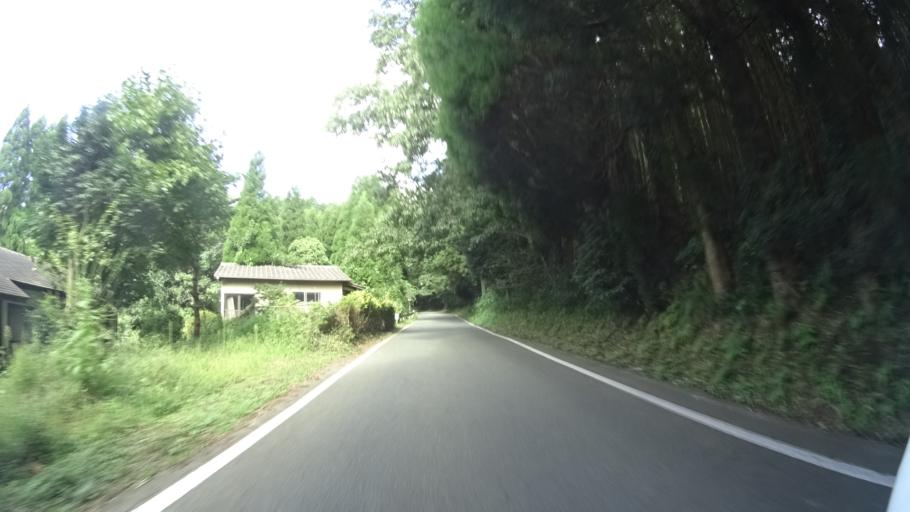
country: JP
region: Kumamoto
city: Aso
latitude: 32.8129
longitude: 131.1321
